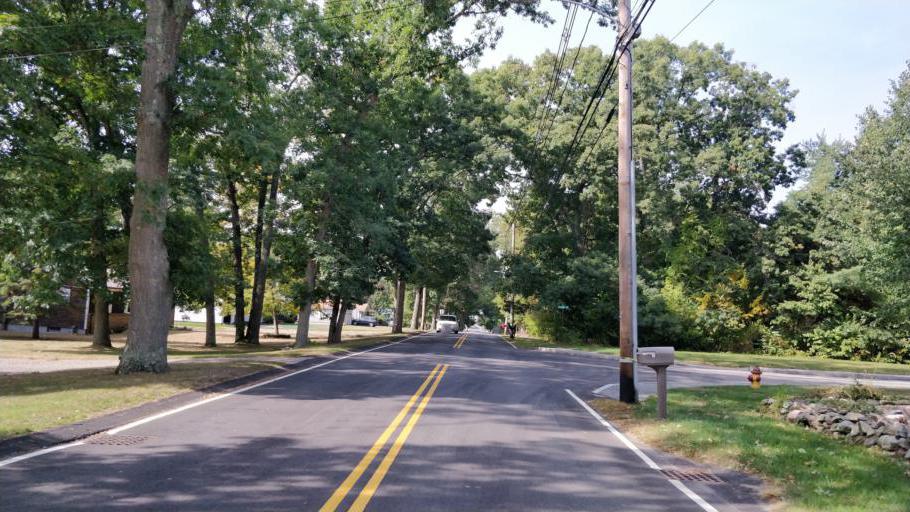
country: US
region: Massachusetts
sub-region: Bristol County
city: North Seekonk
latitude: 41.9038
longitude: -71.3283
